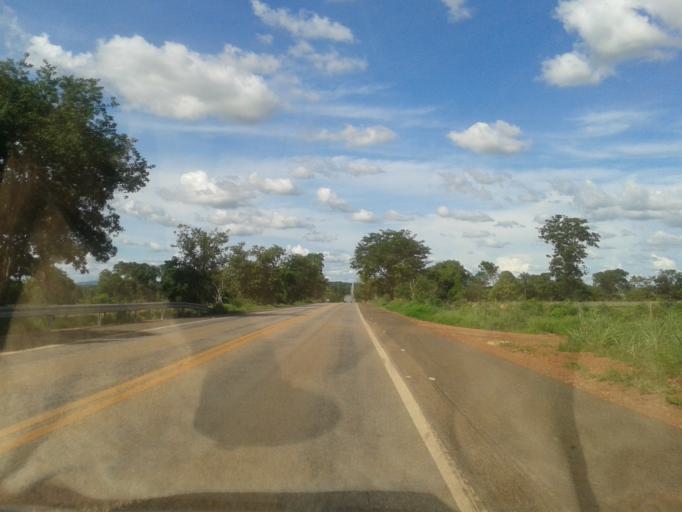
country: BR
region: Goias
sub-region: Mozarlandia
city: Mozarlandia
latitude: -15.0806
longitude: -50.6225
